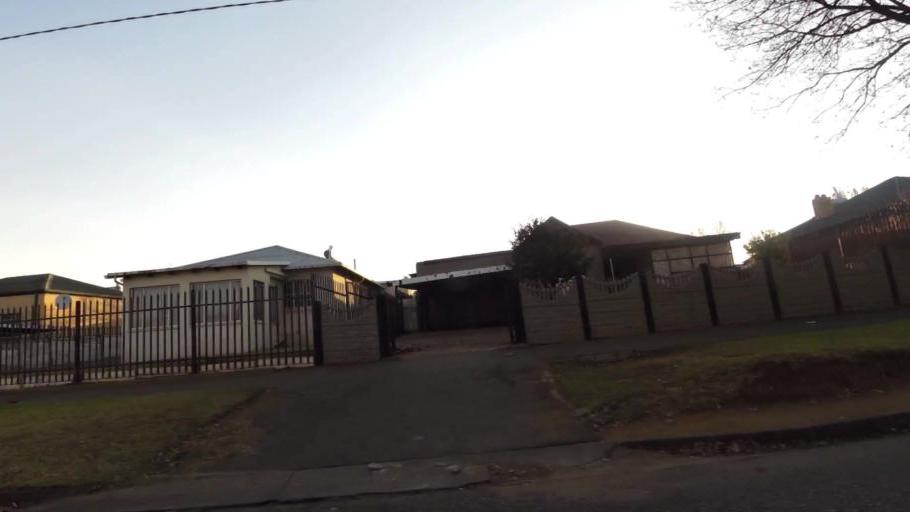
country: ZA
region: Gauteng
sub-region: City of Johannesburg Metropolitan Municipality
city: Johannesburg
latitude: -26.1766
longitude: 27.9622
